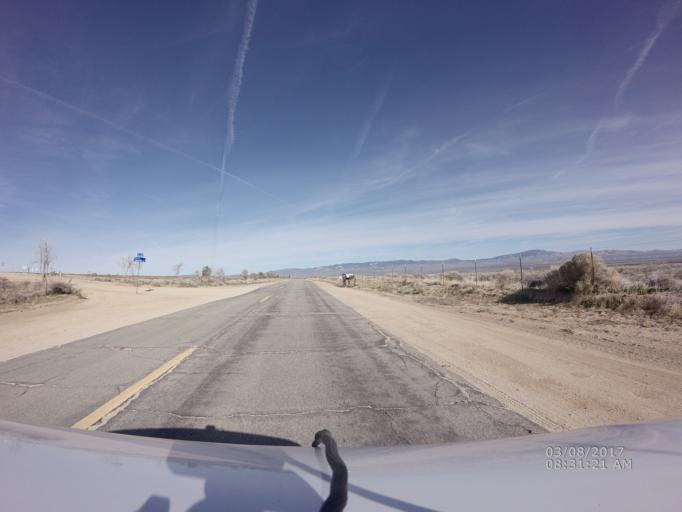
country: US
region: California
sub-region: Los Angeles County
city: Green Valley
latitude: 34.7477
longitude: -118.4862
